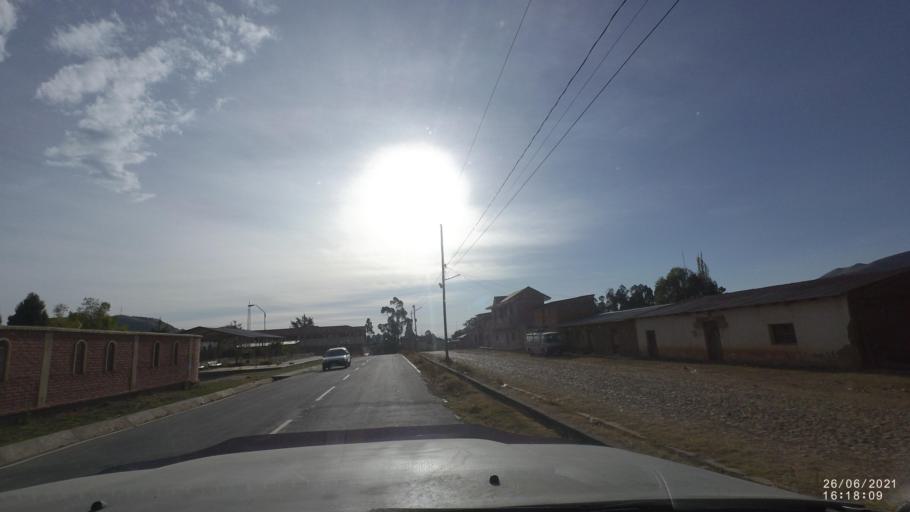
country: BO
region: Cochabamba
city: Arani
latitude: -17.8037
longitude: -65.7999
